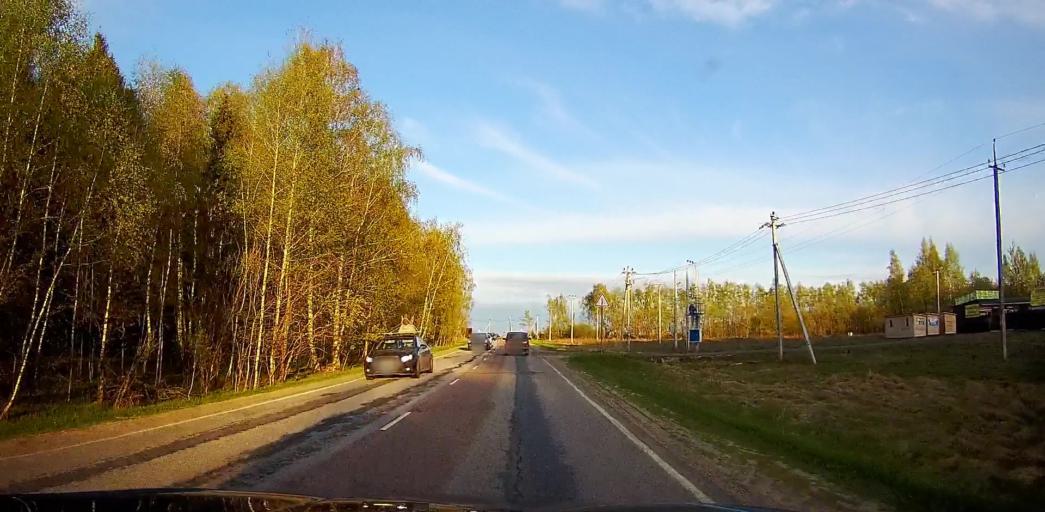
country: RU
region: Moskovskaya
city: Meshcherino
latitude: 55.2238
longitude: 38.3982
